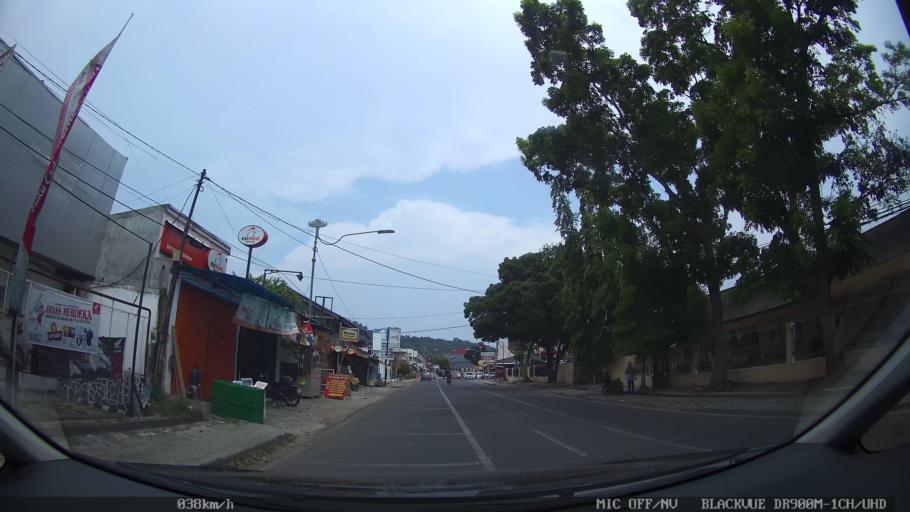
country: ID
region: Lampung
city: Bandarlampung
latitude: -5.4251
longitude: 105.2743
